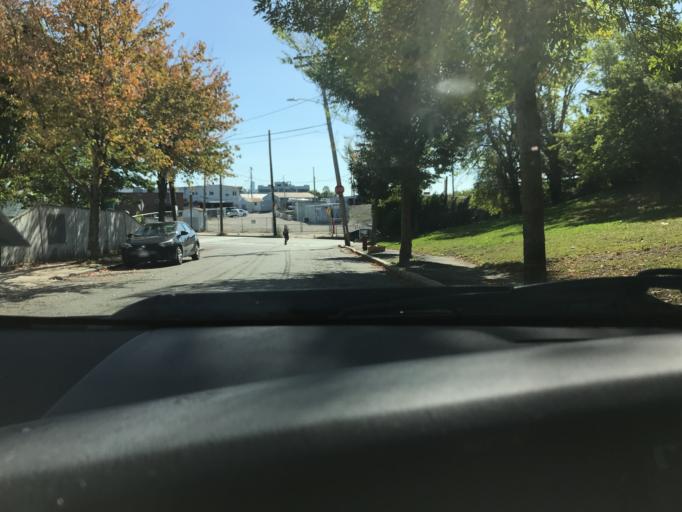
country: US
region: Massachusetts
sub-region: Middlesex County
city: Somerville
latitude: 42.3815
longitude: -71.0880
